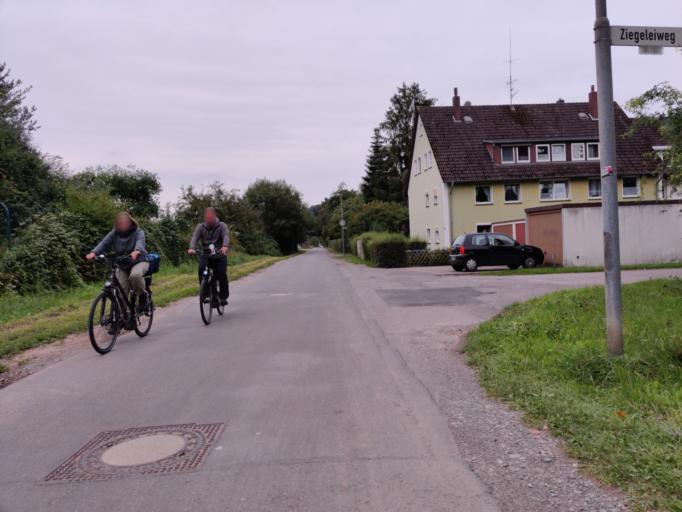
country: DE
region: Lower Saxony
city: Bodenwerder
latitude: 51.9639
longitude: 9.5092
